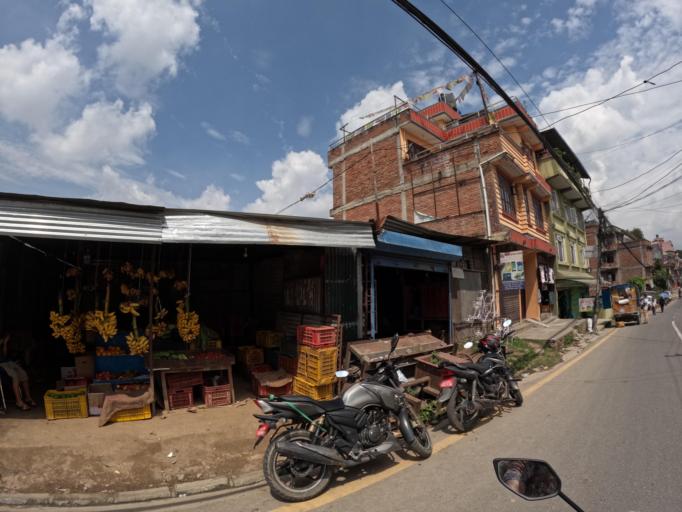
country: NP
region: Central Region
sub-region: Bagmati Zone
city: Bhaktapur
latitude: 27.6777
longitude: 85.3756
